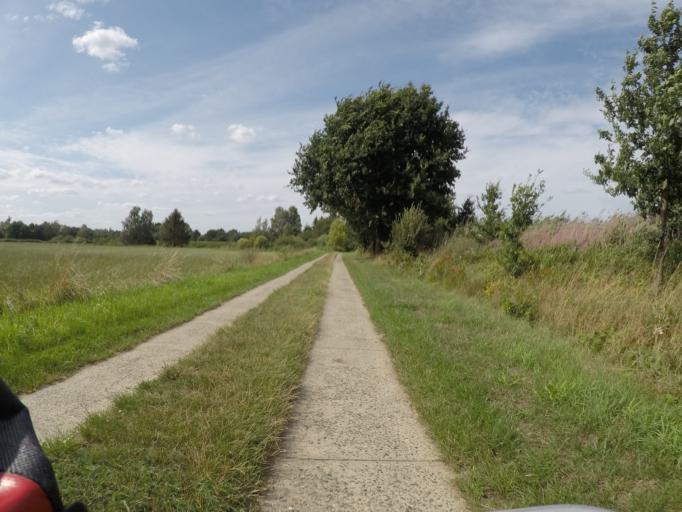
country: DE
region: Lower Saxony
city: Drage
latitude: 53.3674
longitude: 10.2787
